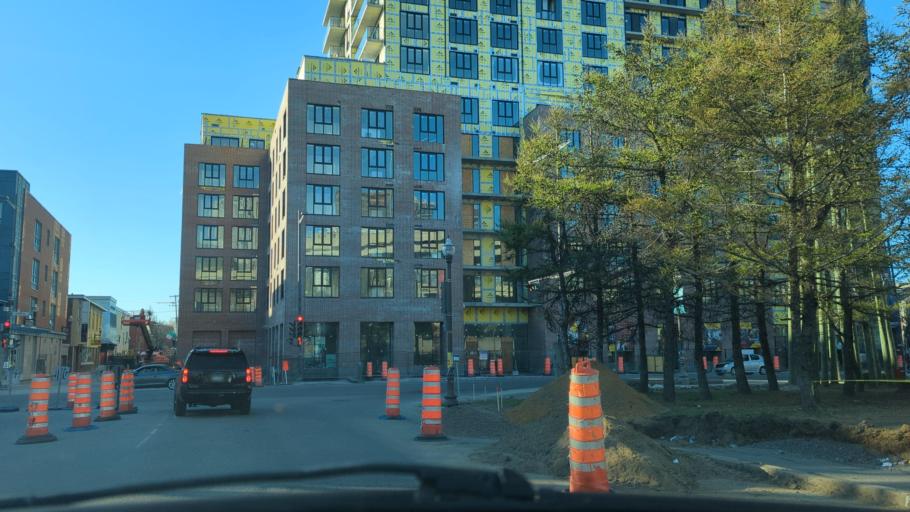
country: CA
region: Quebec
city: Quebec
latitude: 46.8151
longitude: -71.2183
